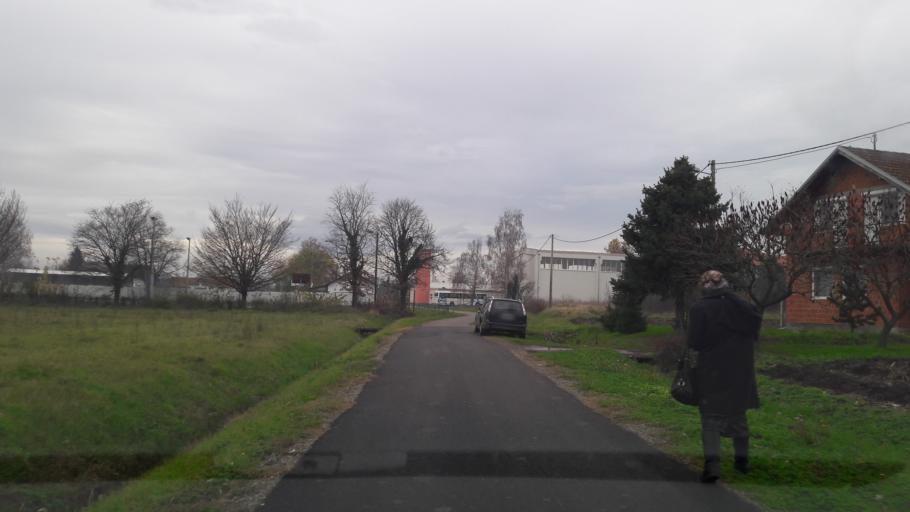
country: HR
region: Osjecko-Baranjska
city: Koska
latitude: 45.5433
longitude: 18.2871
